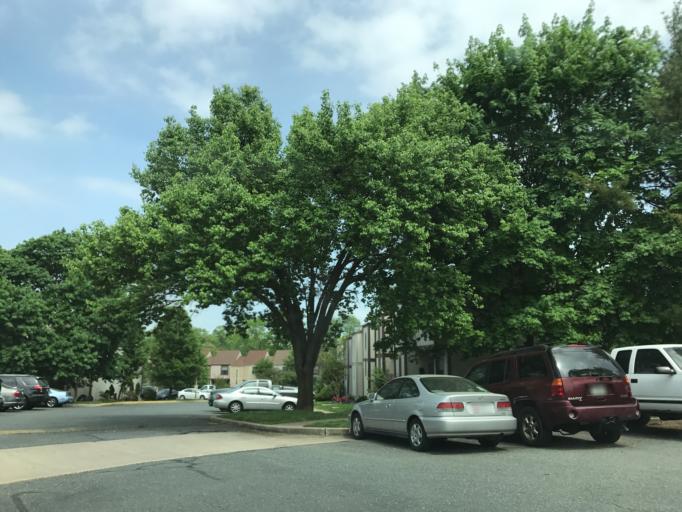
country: US
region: Maryland
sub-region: Baltimore County
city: Middle River
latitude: 39.3134
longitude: -76.4431
